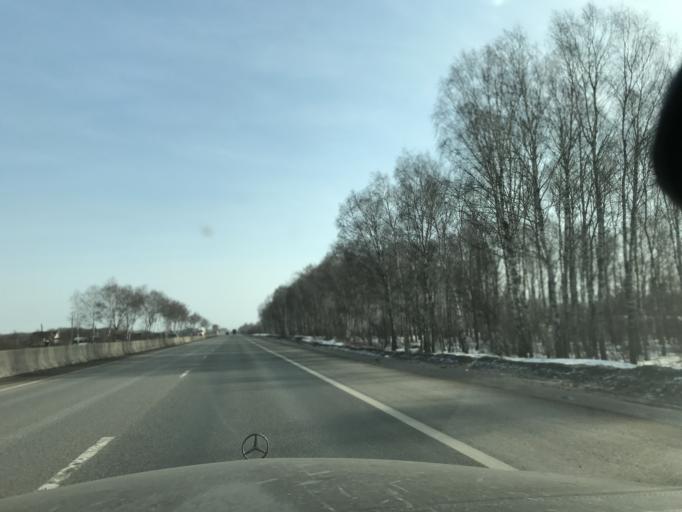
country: RU
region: Nizjnij Novgorod
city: Babino
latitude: 56.3049
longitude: 43.6385
